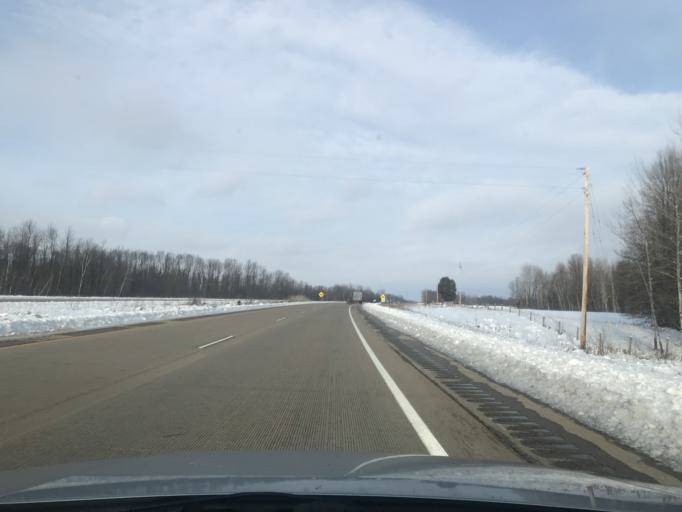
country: US
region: Wisconsin
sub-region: Oconto County
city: Oconto
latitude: 44.9695
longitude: -87.8708
